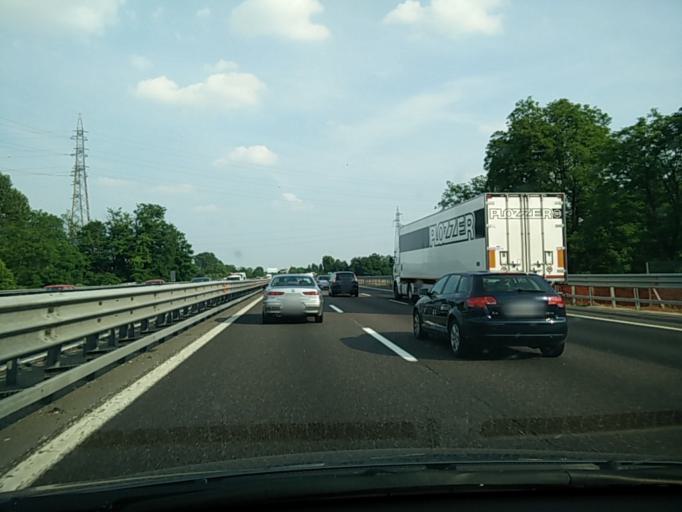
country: IT
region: Lombardy
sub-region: Citta metropolitana di Milano
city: Figino
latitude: 45.4783
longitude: 9.0757
